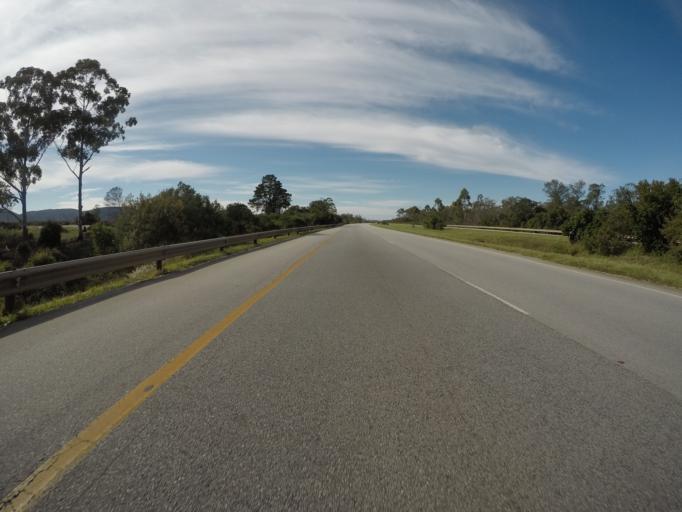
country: ZA
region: Eastern Cape
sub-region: Nelson Mandela Bay Metropolitan Municipality
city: Uitenhage
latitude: -33.9026
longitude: 25.1805
